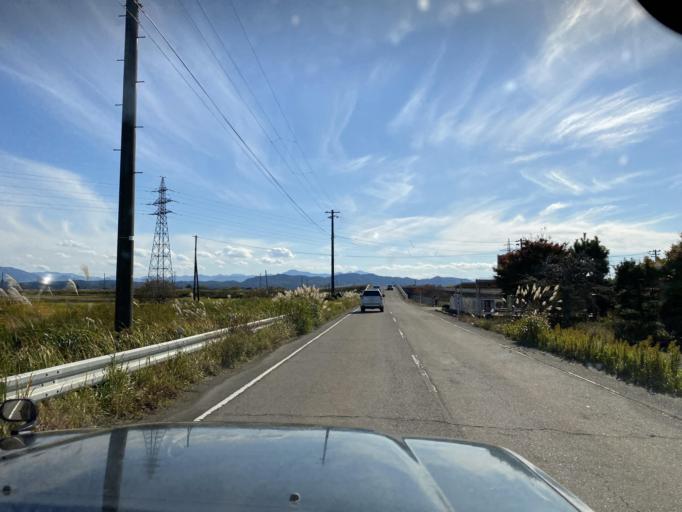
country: JP
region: Niigata
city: Niitsu-honcho
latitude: 37.7905
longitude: 139.0804
